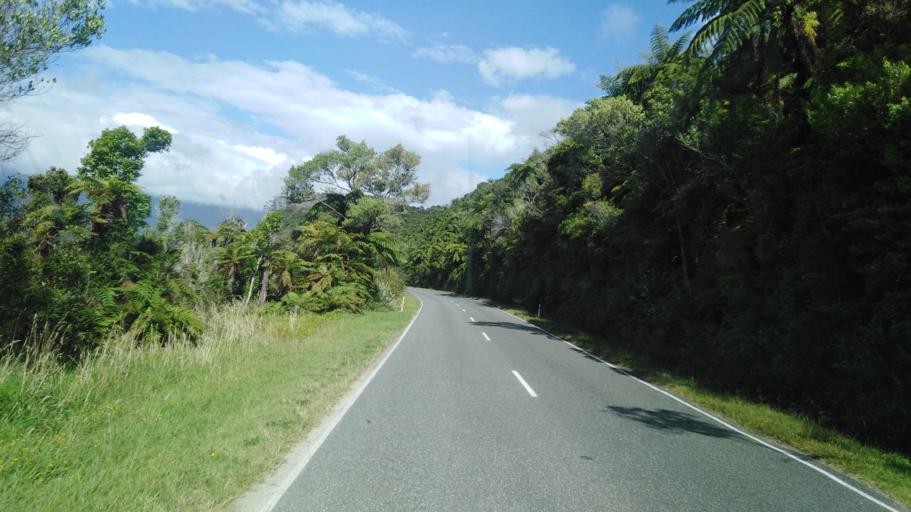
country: NZ
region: West Coast
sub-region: Buller District
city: Westport
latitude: -41.2579
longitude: 172.1176
